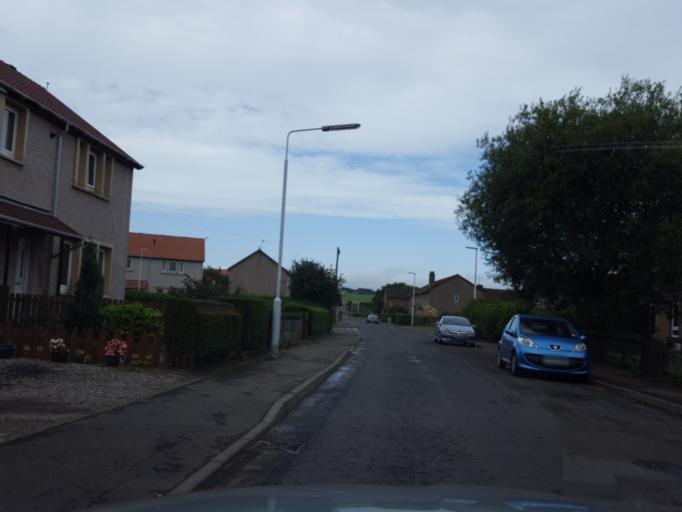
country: GB
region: Scotland
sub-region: Fife
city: Tayport
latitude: 56.4406
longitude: -2.8669
